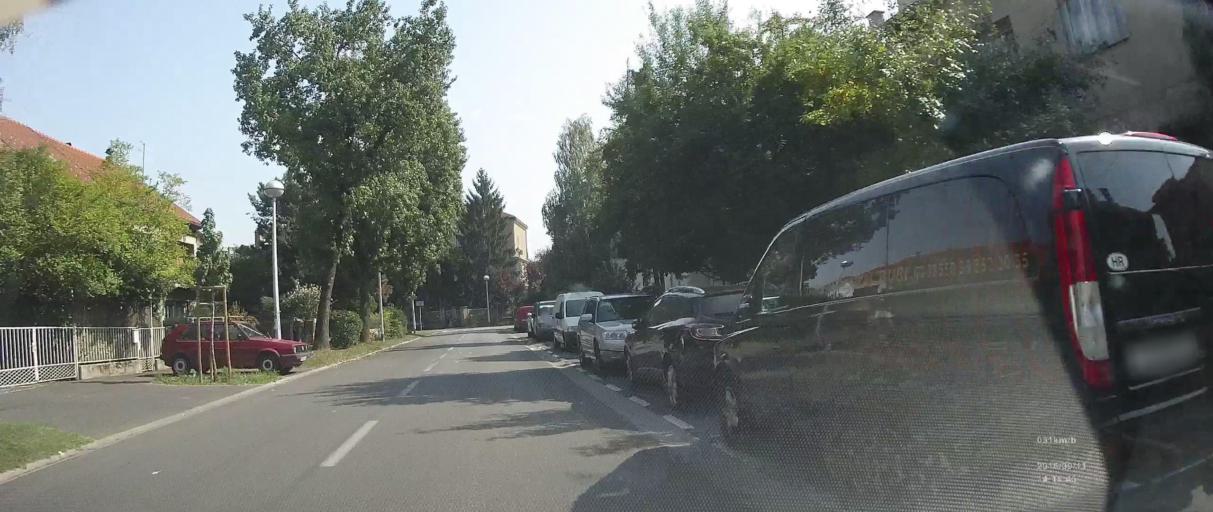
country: HR
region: Grad Zagreb
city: Zagreb
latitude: 45.8164
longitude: 16.0195
